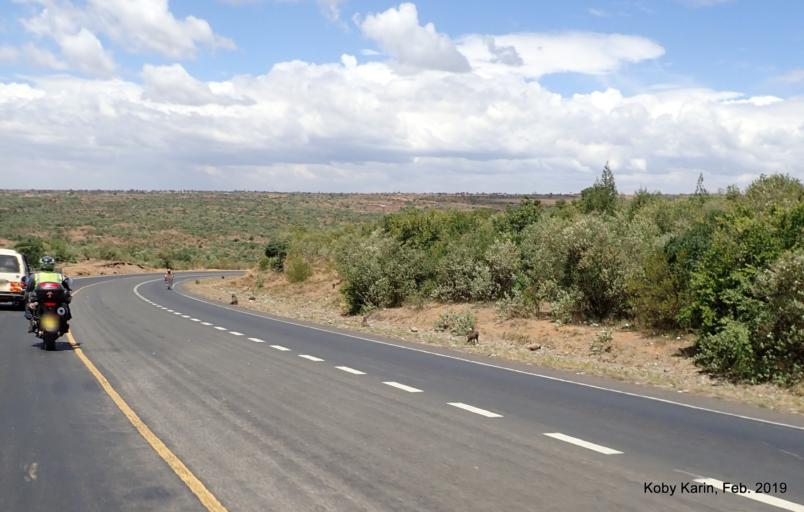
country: KE
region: Narok
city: Narok
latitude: -1.1141
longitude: 36.0470
